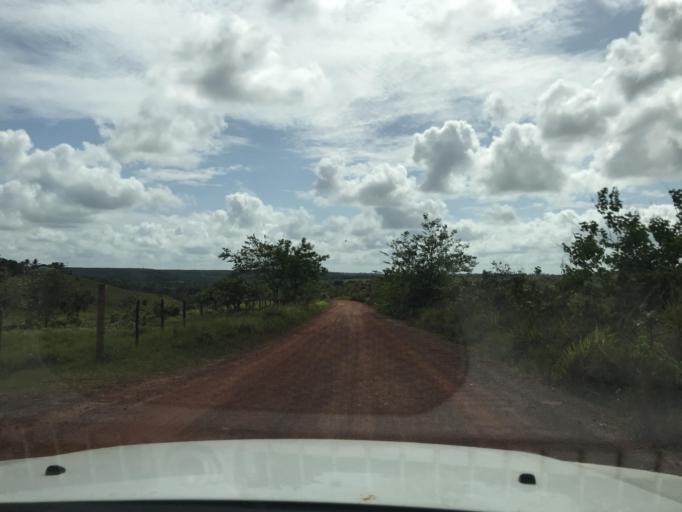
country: BR
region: Bahia
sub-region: Entre Rios
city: Entre Rios
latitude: -12.1706
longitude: -38.0991
